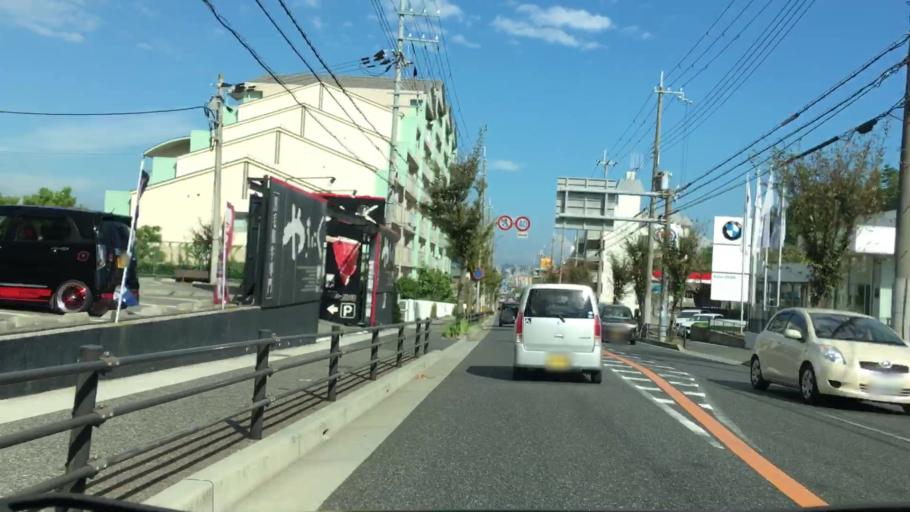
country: JP
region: Hyogo
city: Akashi
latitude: 34.6695
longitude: 134.9734
